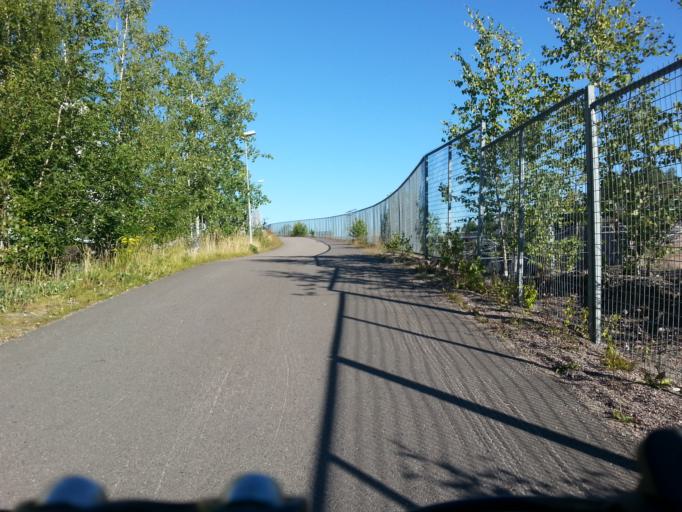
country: FI
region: Uusimaa
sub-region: Helsinki
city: Helsinki
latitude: 60.2055
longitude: 24.9250
